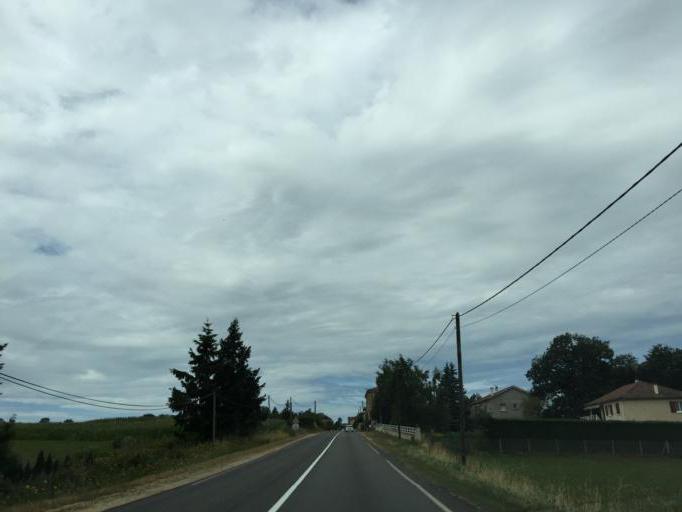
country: FR
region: Rhone-Alpes
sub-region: Departement de la Loire
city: Saint-Maurice-en-Gourgois
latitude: 45.4093
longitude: 4.2053
